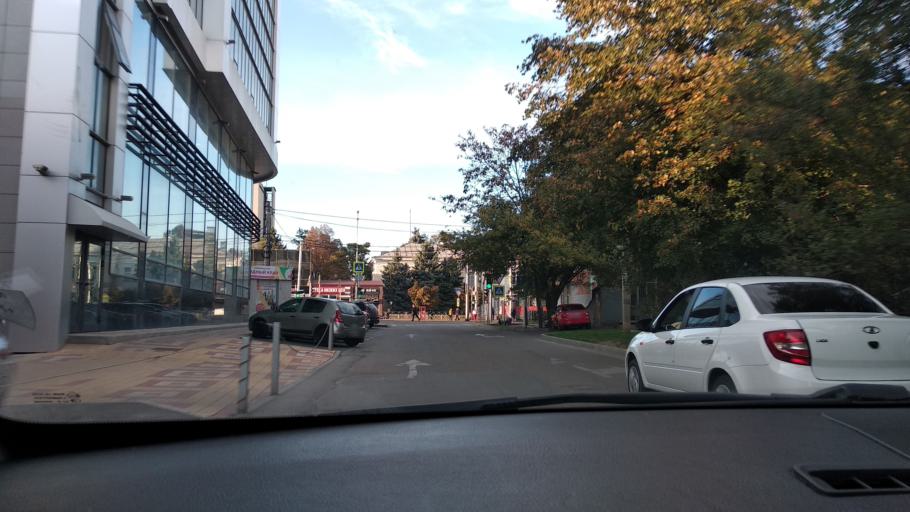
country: RU
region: Krasnodarskiy
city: Krasnodar
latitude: 45.0196
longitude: 39.0043
